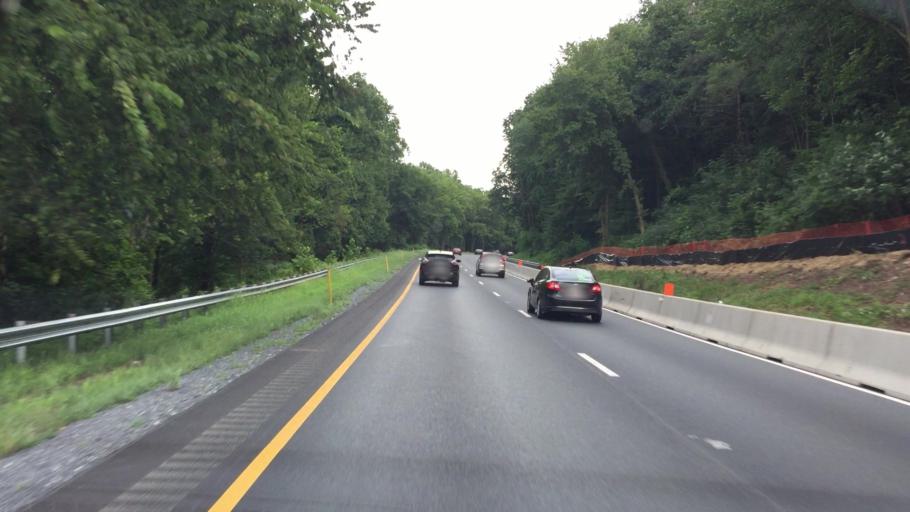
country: US
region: Maryland
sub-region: Frederick County
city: Green Valley
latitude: 39.2733
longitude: -77.3183
